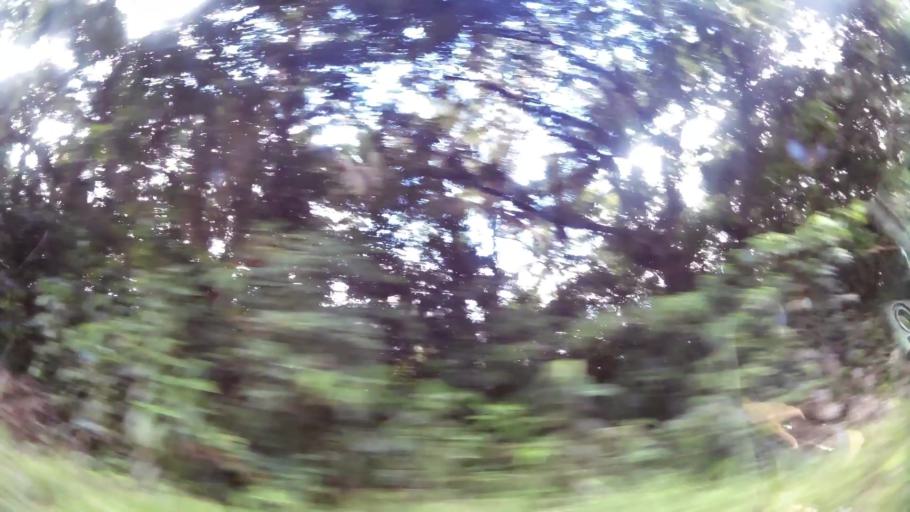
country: DM
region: Saint Andrew
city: Calibishie
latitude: 15.5932
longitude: -61.3674
